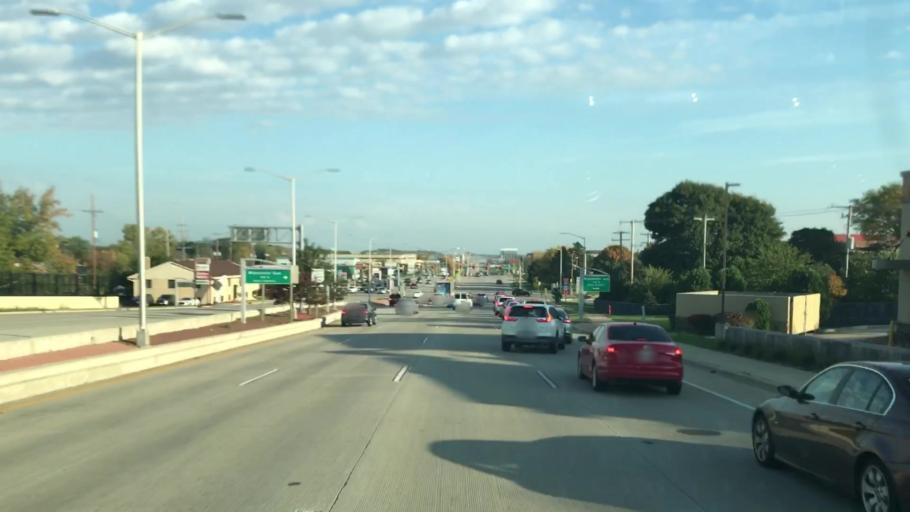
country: US
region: Wisconsin
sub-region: Waukesha County
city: Elm Grove
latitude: 43.0366
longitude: -88.0469
